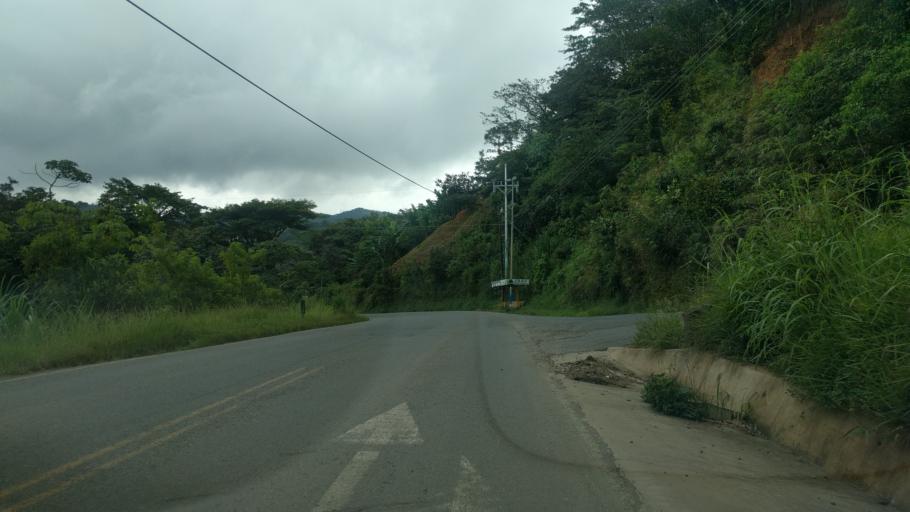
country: CR
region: Alajuela
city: San Rafael
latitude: 10.0311
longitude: -84.5119
